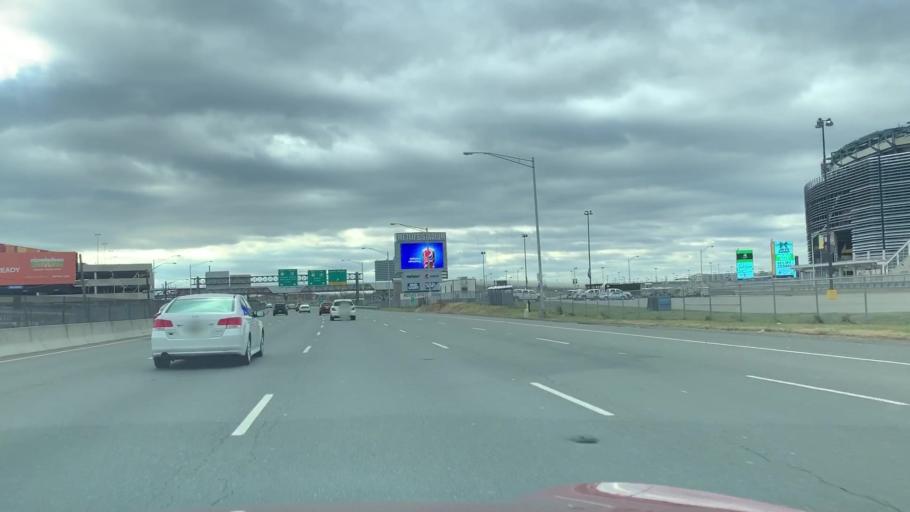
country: US
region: New Jersey
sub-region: Hudson County
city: Secaucus
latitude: 40.8138
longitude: -74.0697
